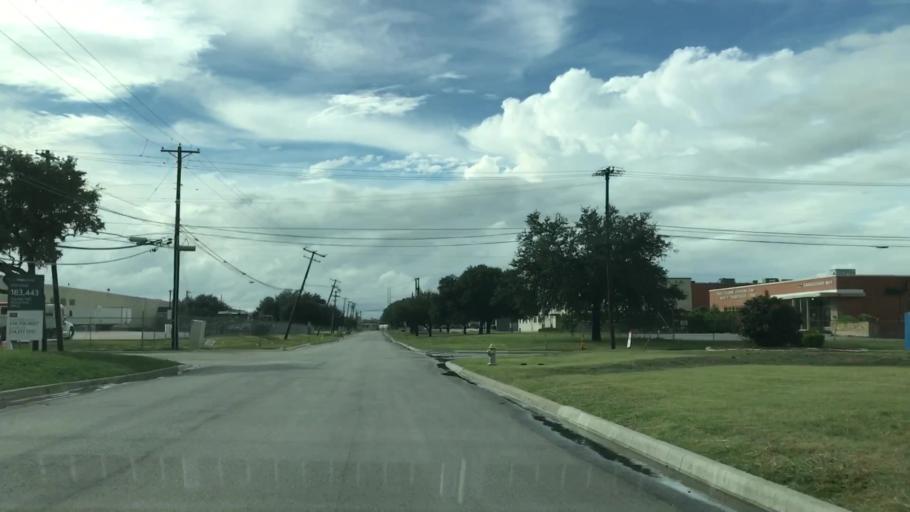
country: US
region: Texas
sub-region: Dallas County
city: Irving
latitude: 32.8221
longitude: -96.8830
